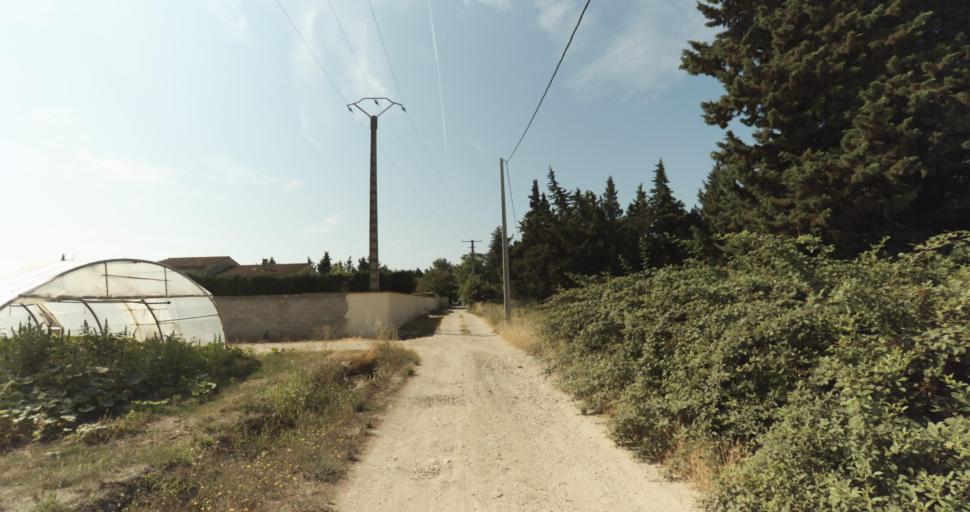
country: FR
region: Provence-Alpes-Cote d'Azur
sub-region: Departement du Vaucluse
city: Monteux
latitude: 44.0270
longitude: 5.0242
